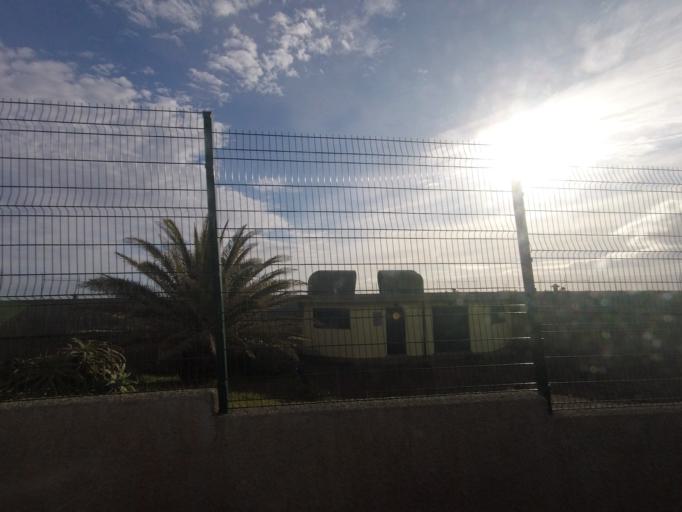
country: PT
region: Madeira
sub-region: Machico
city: Canical
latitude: 32.7471
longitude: -16.7397
